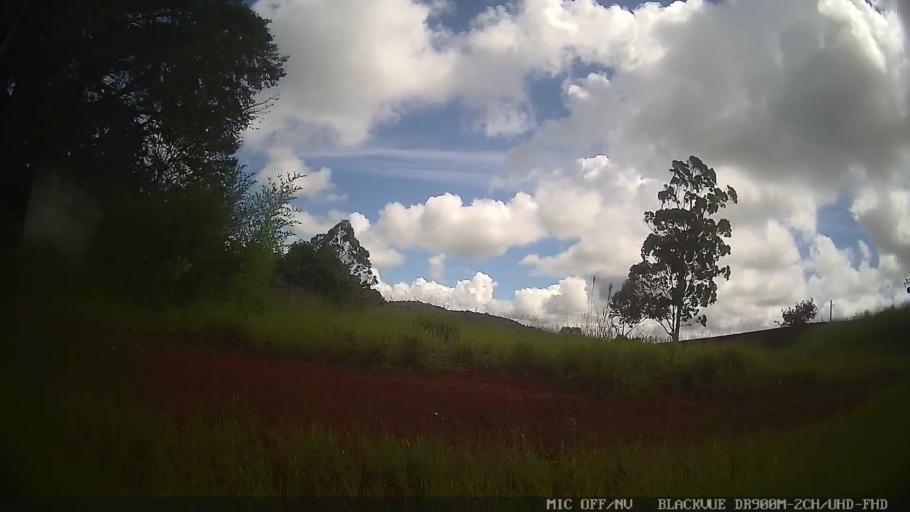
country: BR
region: Sao Paulo
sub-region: Braganca Paulista
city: Braganca Paulista
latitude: -22.8624
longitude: -46.6351
